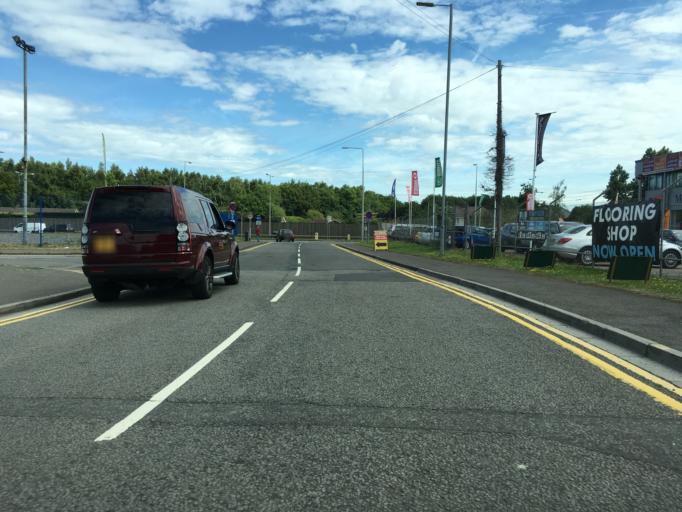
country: GB
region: Wales
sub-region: Newport
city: Nash
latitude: 51.5745
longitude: -2.9632
